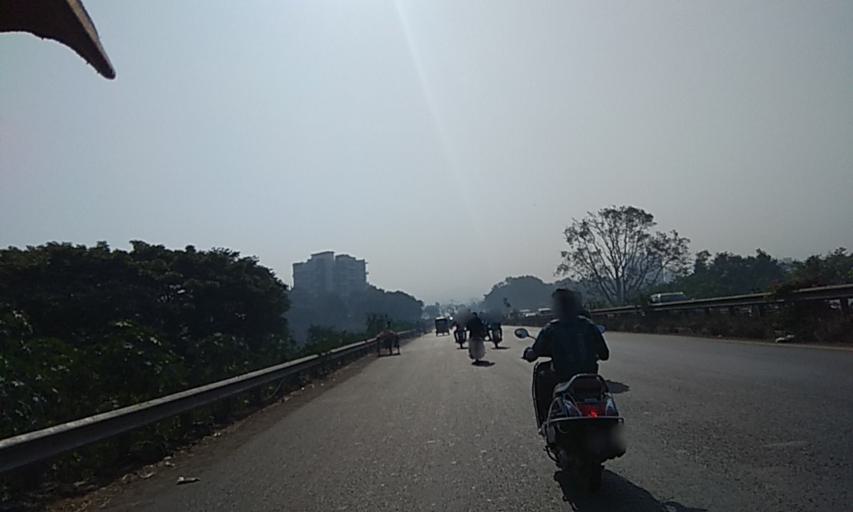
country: IN
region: Maharashtra
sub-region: Pune Division
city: Kharakvasla
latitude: 18.4759
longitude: 73.8084
